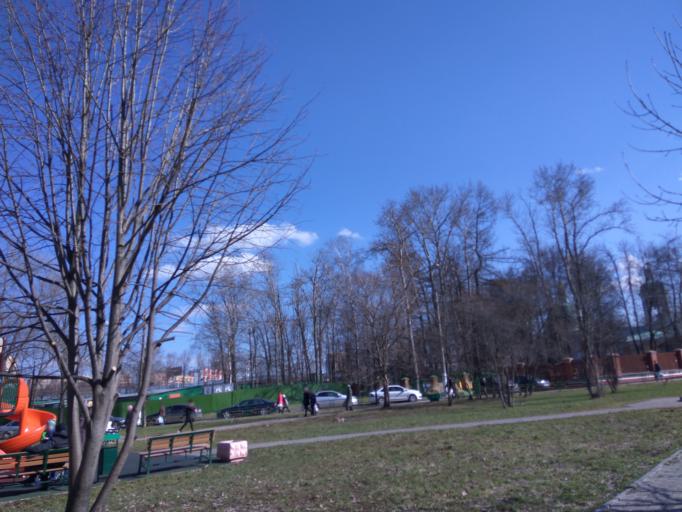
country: RU
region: Moscow
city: Ivanovskoye
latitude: 55.7703
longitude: 37.8383
